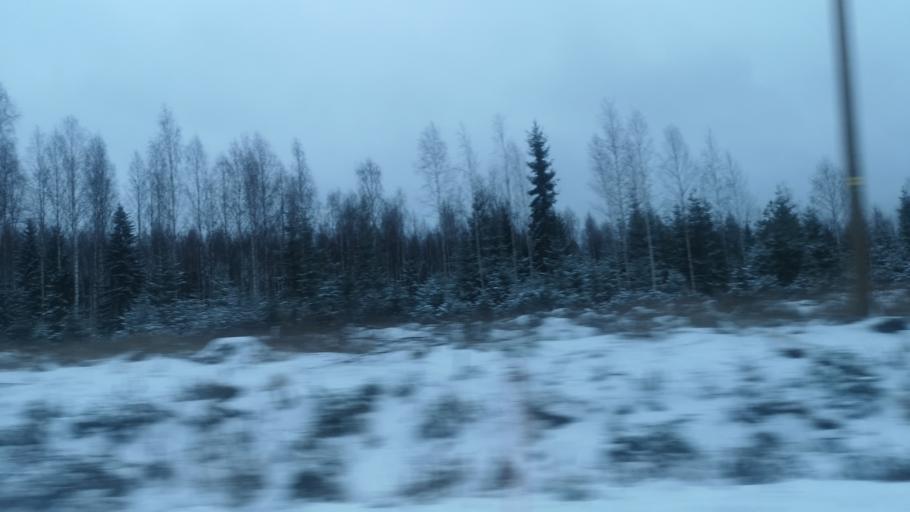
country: FI
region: Southern Savonia
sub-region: Savonlinna
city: Enonkoski
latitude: 62.0310
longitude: 28.7214
